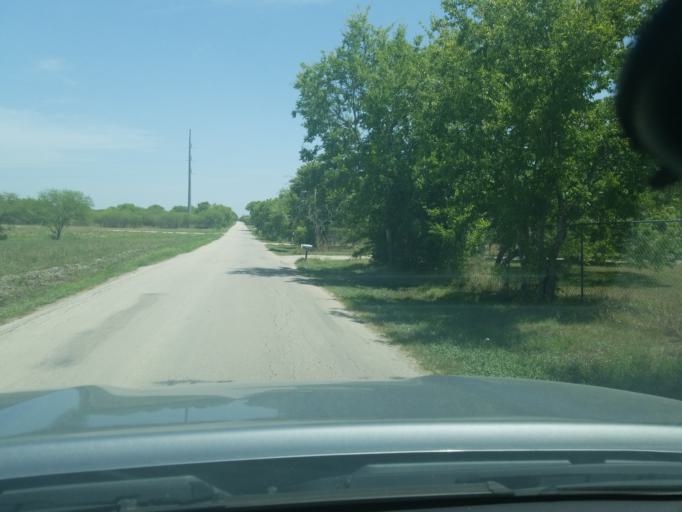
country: US
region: Texas
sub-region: Guadalupe County
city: Cibolo
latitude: 29.5838
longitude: -98.2006
